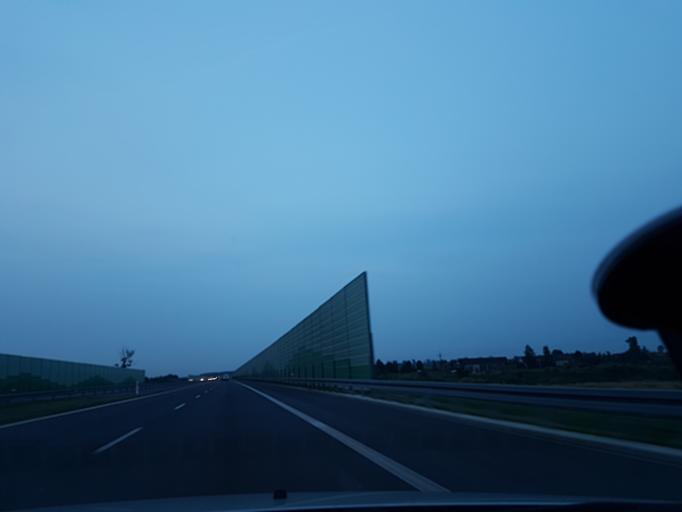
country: PL
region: Lodz Voivodeship
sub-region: Powiat leczycki
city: Piatek
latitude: 52.0925
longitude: 19.5190
